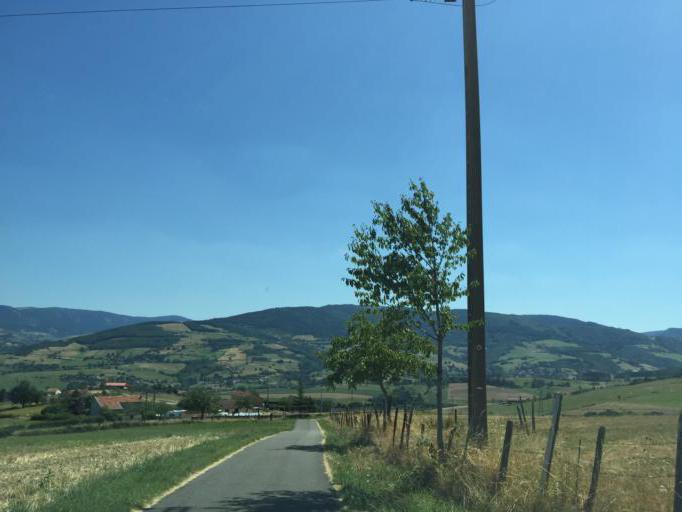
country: FR
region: Rhone-Alpes
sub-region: Departement de la Loire
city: Saint-Jean-Bonnefonds
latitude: 45.4700
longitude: 4.4691
